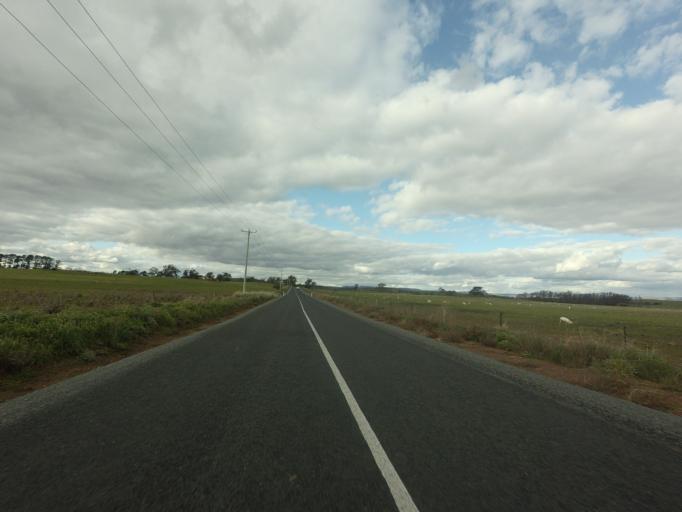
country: AU
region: Tasmania
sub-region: Northern Midlands
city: Evandale
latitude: -41.9103
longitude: 147.3819
